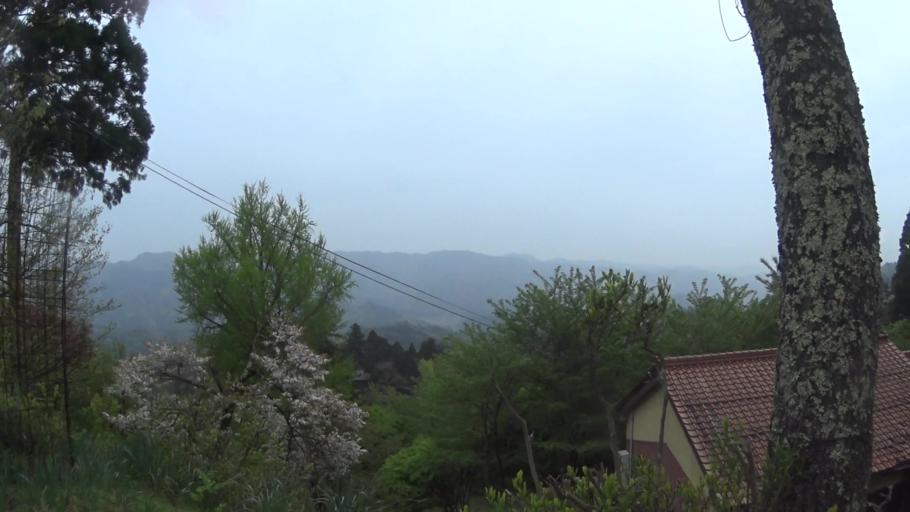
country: JP
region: Kyoto
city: Maizuru
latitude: 35.3892
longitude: 135.4424
